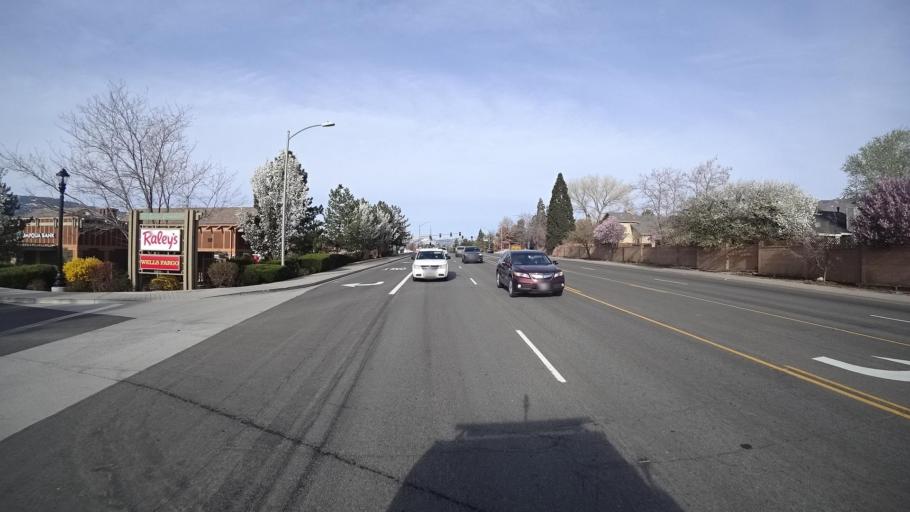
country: US
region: Nevada
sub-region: Washoe County
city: Mogul
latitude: 39.5296
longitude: -119.8806
